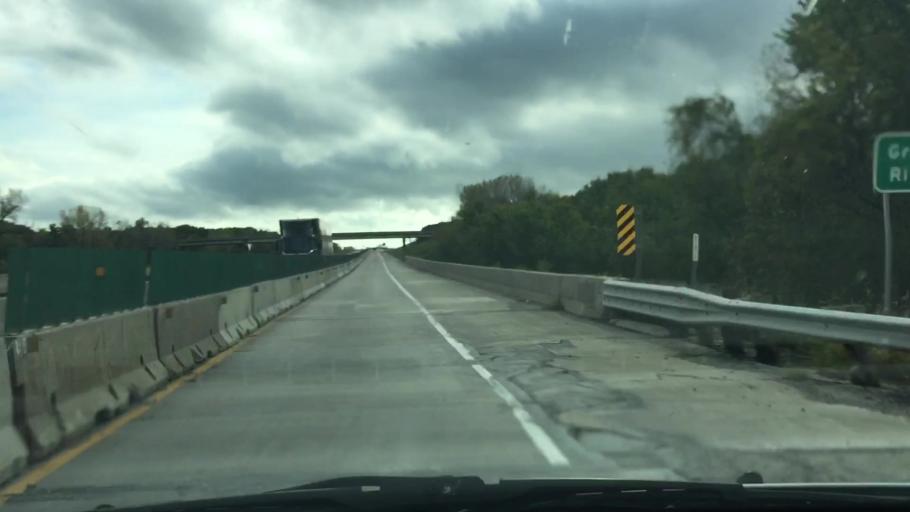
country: US
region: Iowa
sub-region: Decatur County
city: Lamoni
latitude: 40.6600
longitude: -93.8558
